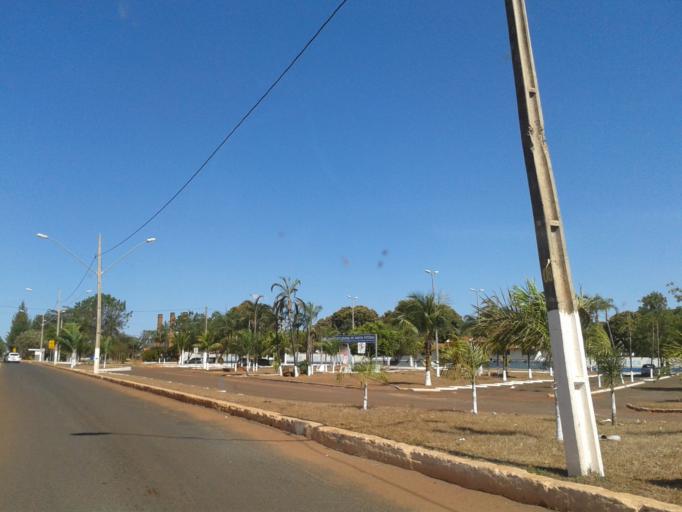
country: BR
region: Minas Gerais
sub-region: Santa Vitoria
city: Santa Vitoria
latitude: -18.8544
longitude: -50.1305
